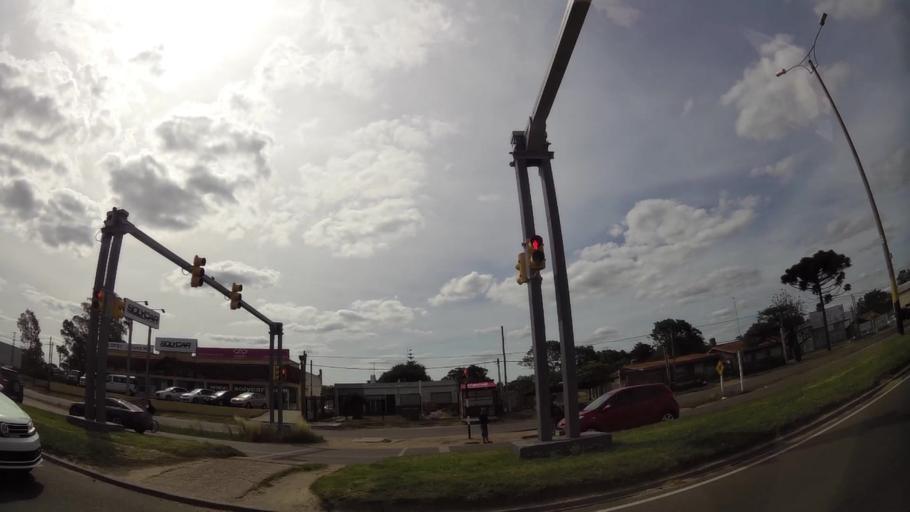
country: UY
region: Canelones
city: Barra de Carrasco
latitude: -34.8314
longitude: -55.9754
